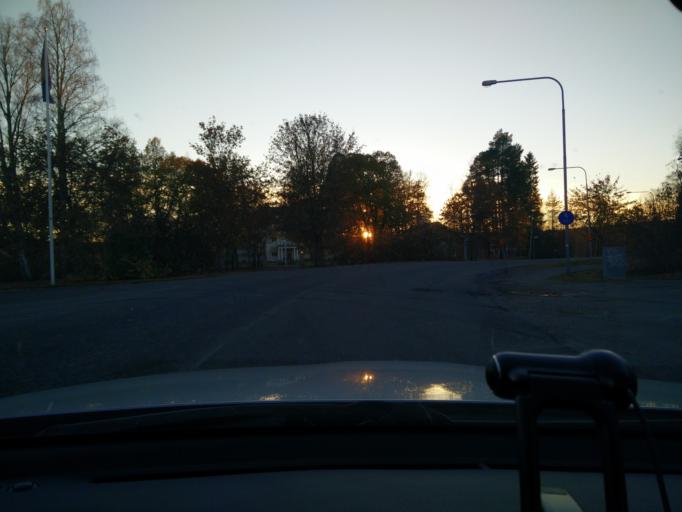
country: SE
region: Vaesternorrland
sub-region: Sundsvalls Kommun
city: Matfors
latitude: 62.3483
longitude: 17.0308
